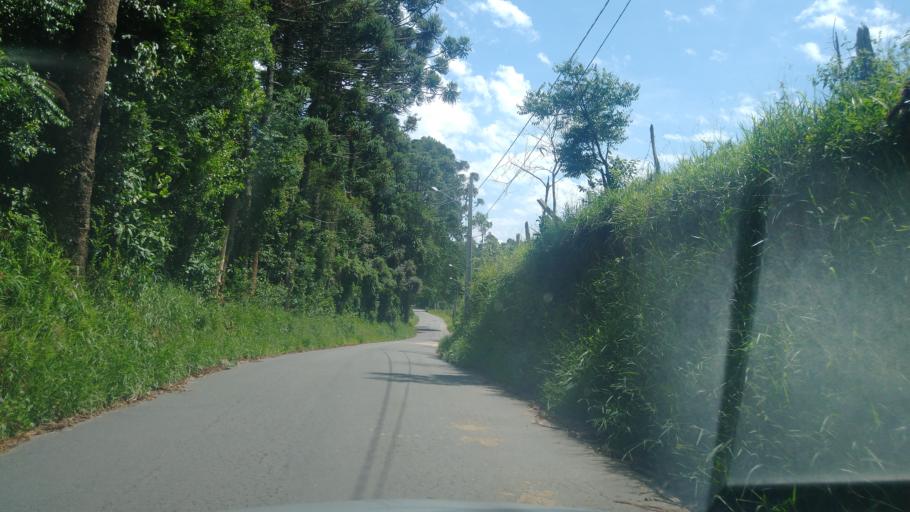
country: BR
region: Minas Gerais
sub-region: Extrema
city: Extrema
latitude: -22.7865
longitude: -46.2881
